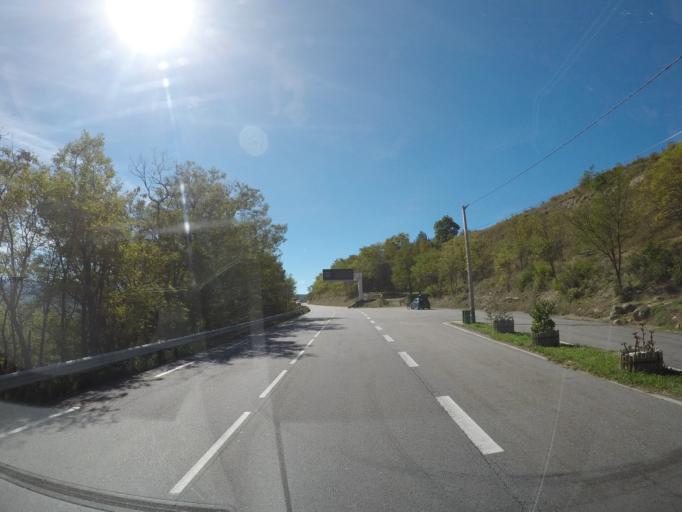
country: FR
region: Languedoc-Roussillon
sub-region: Departement des Pyrenees-Orientales
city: la Guingueta d'Ix
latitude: 42.4579
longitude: 1.9358
